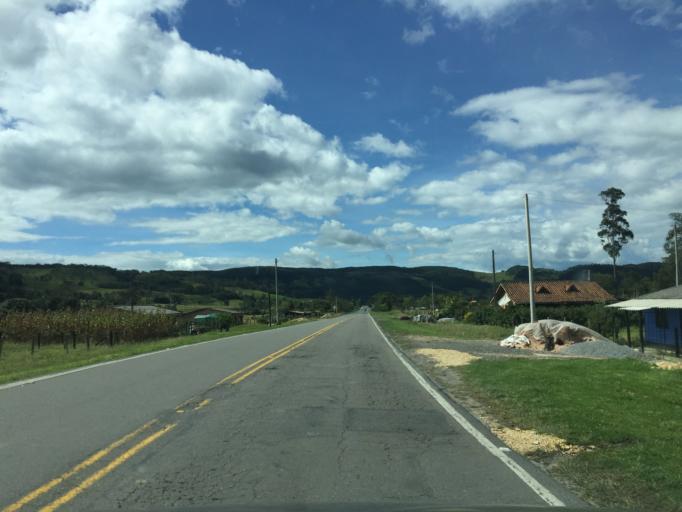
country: CO
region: Boyaca
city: Arcabuco
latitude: 5.7754
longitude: -73.4587
